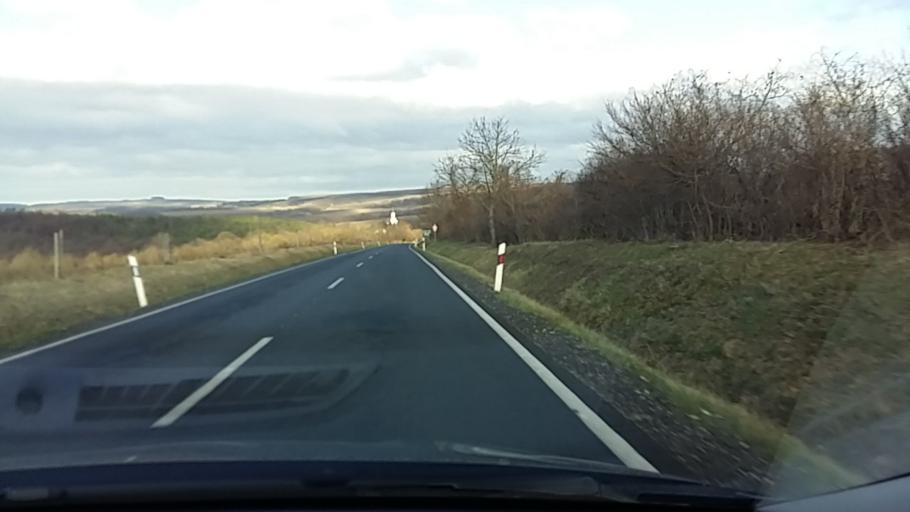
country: HU
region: Veszprem
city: Urkut
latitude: 46.9935
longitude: 17.6612
